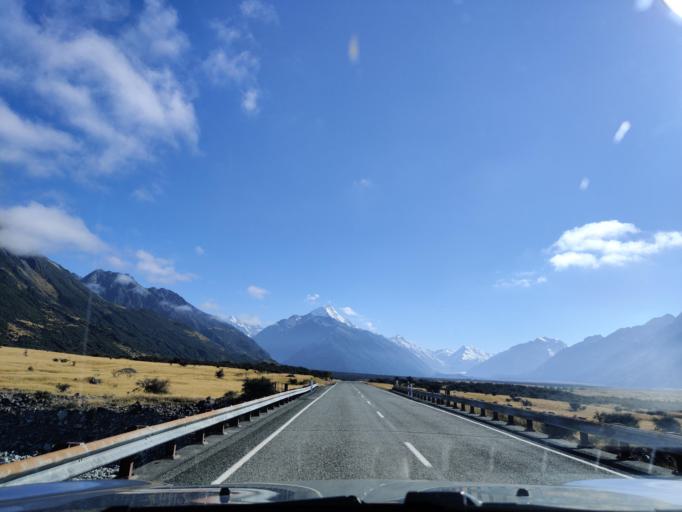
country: NZ
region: Canterbury
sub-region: Timaru District
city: Pleasant Point
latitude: -43.8020
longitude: 170.1136
